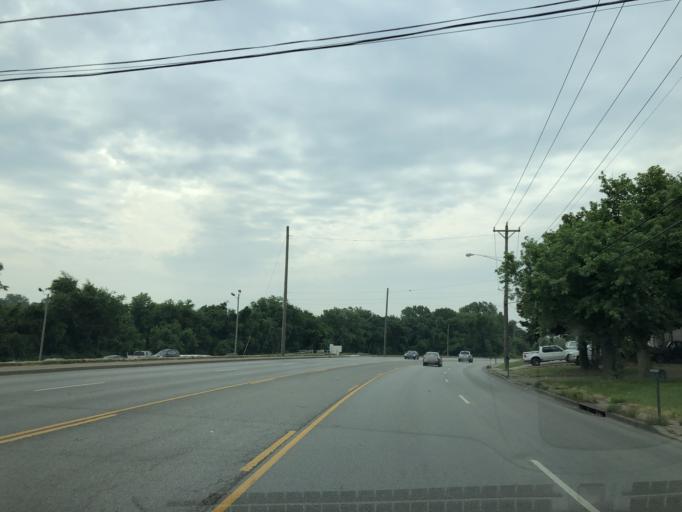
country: US
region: Tennessee
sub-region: Davidson County
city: Oak Hill
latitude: 36.0782
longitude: -86.6830
